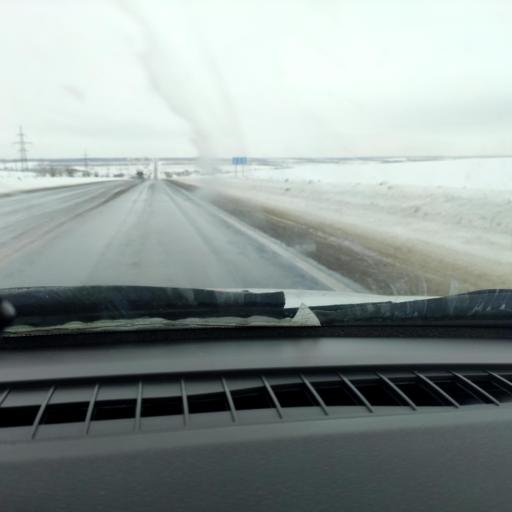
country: RU
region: Samara
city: Novokuybyshevsk
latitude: 53.0099
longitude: 50.0382
